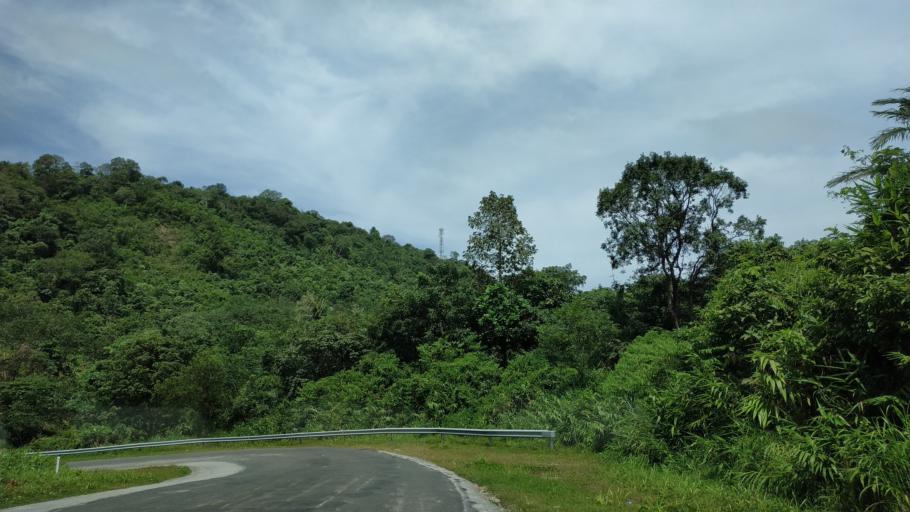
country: MM
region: Tanintharyi
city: Dawei
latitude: 14.1360
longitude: 98.1174
